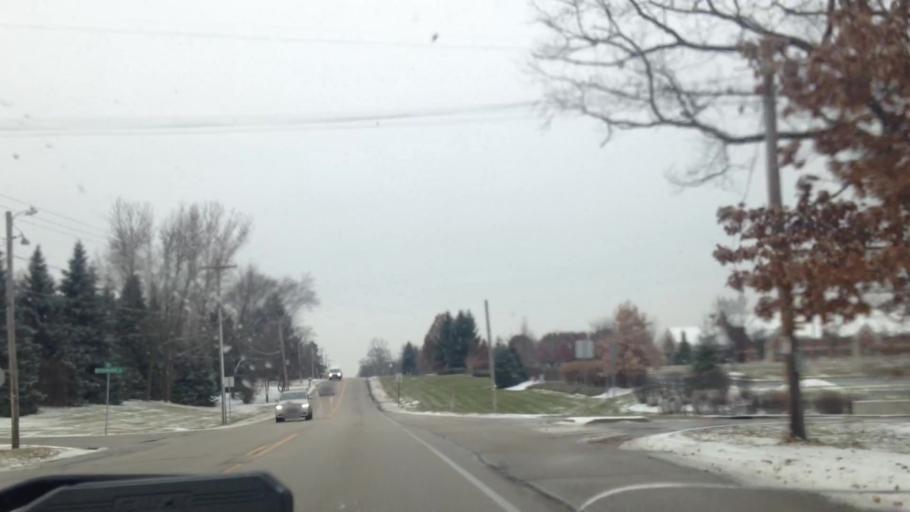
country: US
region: Wisconsin
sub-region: Waukesha County
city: Brookfield
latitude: 43.0966
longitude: -88.1056
